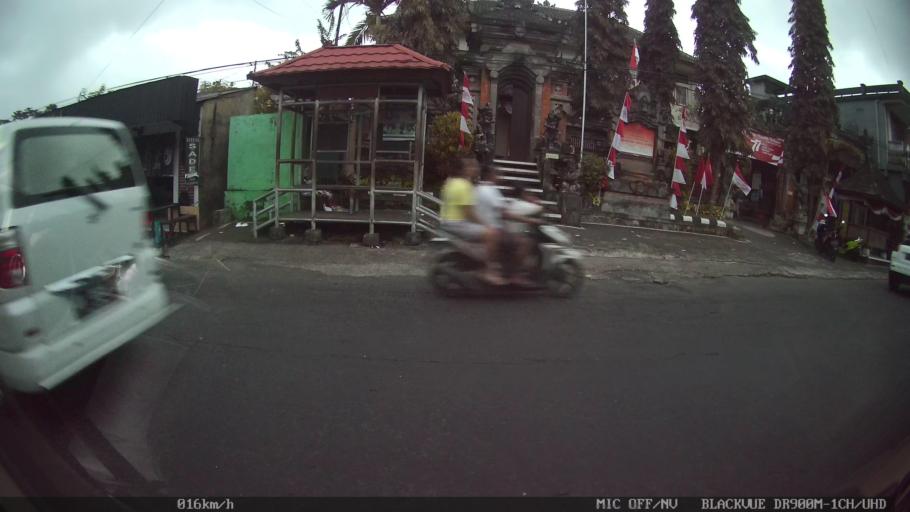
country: ID
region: Bali
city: Banjar Tengah
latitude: -8.4538
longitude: 115.2800
